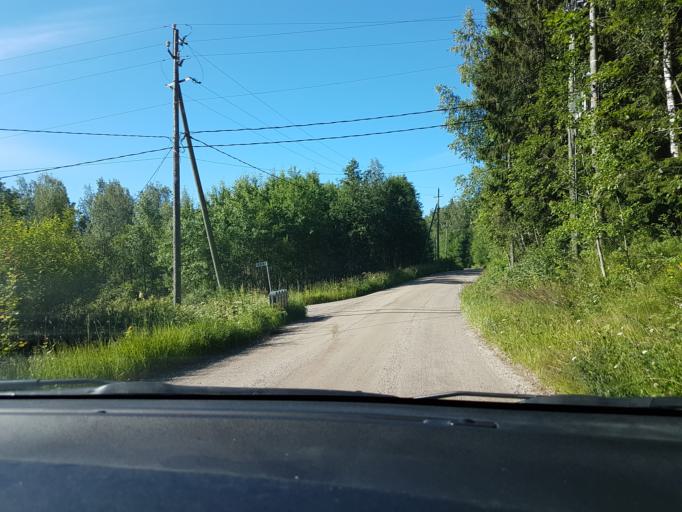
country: FI
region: Uusimaa
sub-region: Helsinki
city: Sibbo
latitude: 60.2853
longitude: 25.2401
